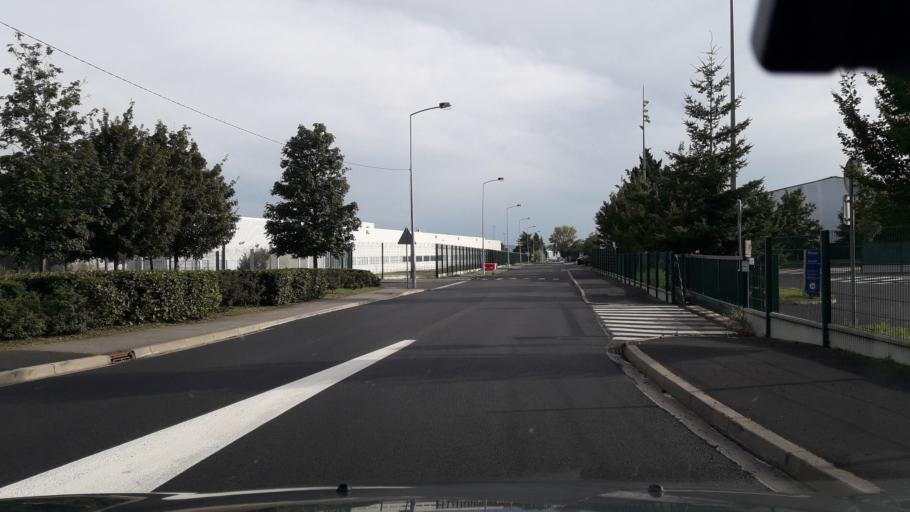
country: FR
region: Auvergne
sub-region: Departement du Puy-de-Dome
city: Cebazat
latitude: 45.8429
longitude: 3.1205
